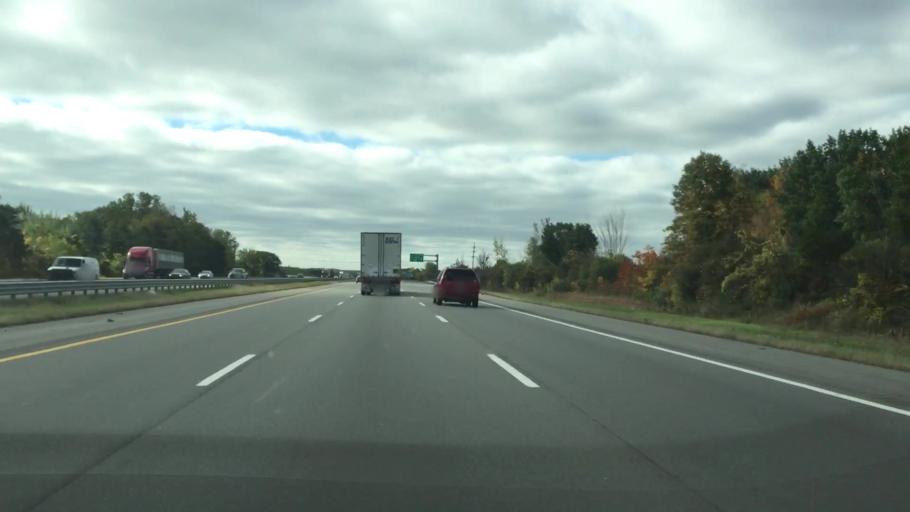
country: US
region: Michigan
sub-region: Macomb County
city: Mount Clemens
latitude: 42.6519
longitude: -82.8367
